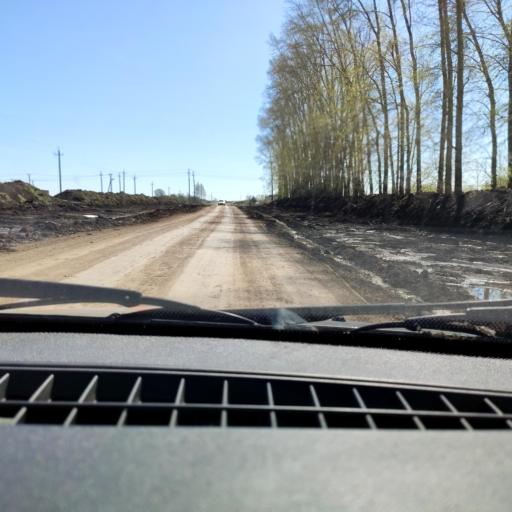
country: RU
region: Bashkortostan
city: Iglino
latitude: 54.8155
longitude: 56.4330
